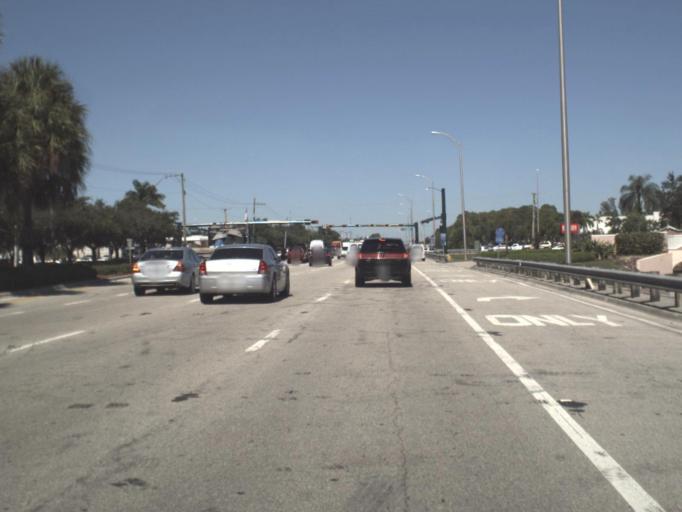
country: US
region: Florida
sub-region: Collier County
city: Pine Ridge
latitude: 26.2099
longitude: -81.7683
